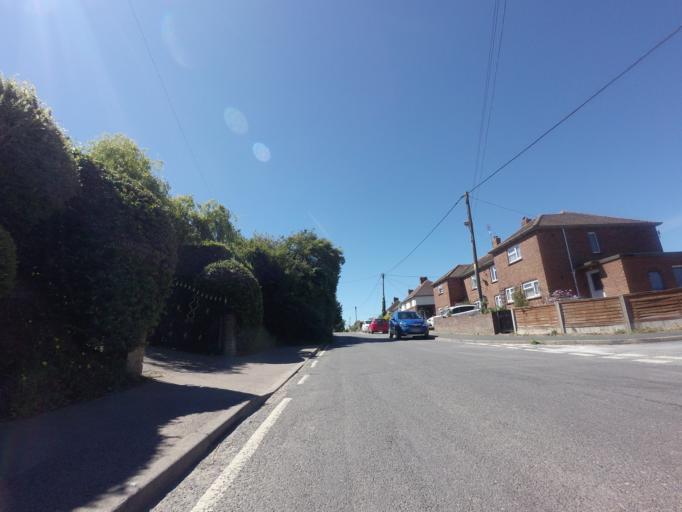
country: GB
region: England
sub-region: Kent
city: Eastry
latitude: 51.2455
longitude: 1.3000
